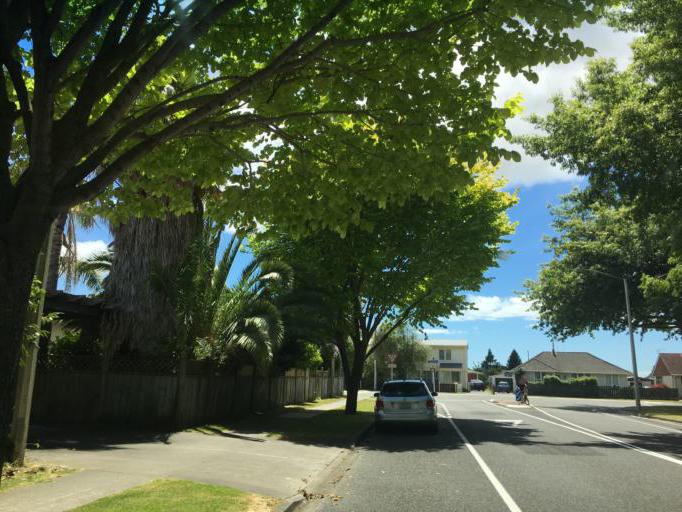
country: NZ
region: Hawke's Bay
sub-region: Hastings District
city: Hastings
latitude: -39.6424
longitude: 176.8625
